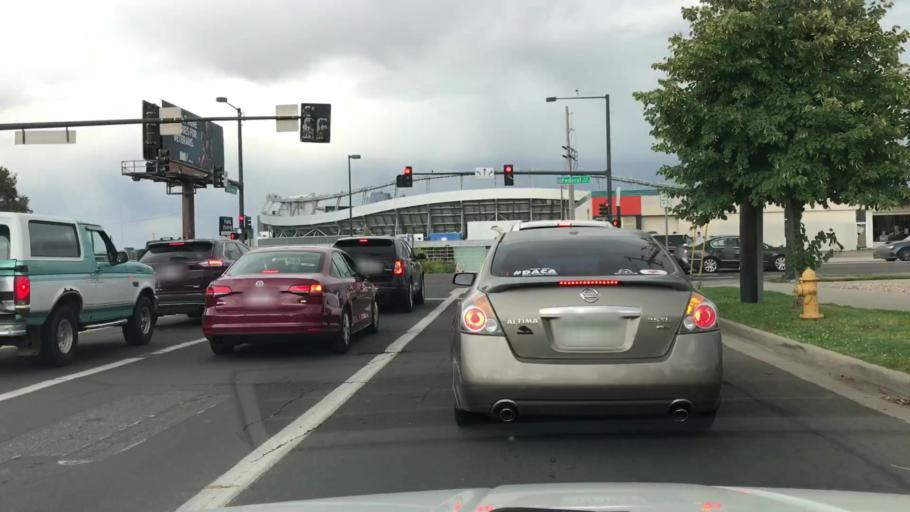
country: US
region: Colorado
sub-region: Jefferson County
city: Edgewater
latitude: 39.7439
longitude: -105.0257
